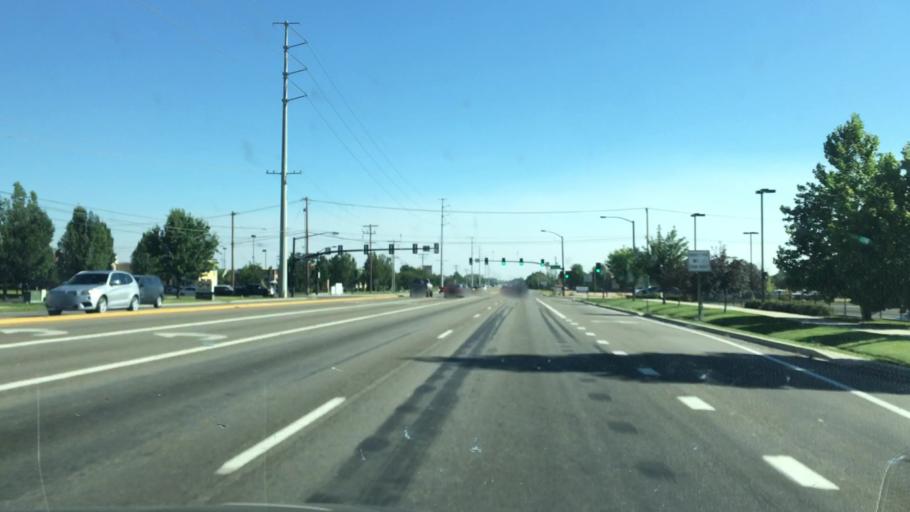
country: US
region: Idaho
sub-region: Ada County
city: Meridian
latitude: 43.6350
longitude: -116.3544
